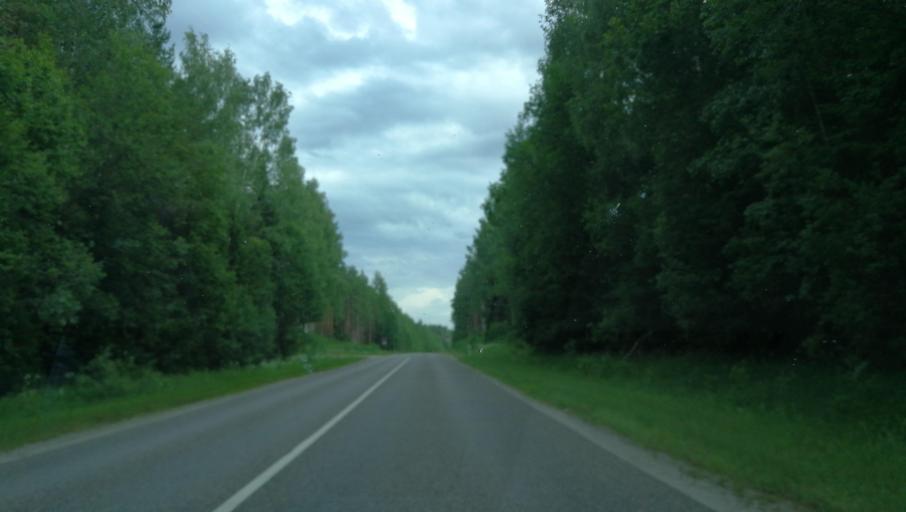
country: LV
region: Naukseni
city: Naukseni
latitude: 57.8023
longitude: 25.4141
